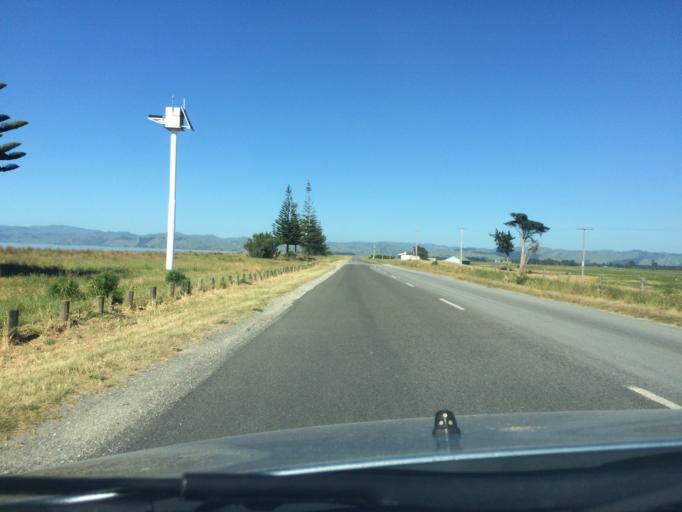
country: NZ
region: Gisborne
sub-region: Gisborne District
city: Gisborne
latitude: -38.6744
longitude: 177.9883
